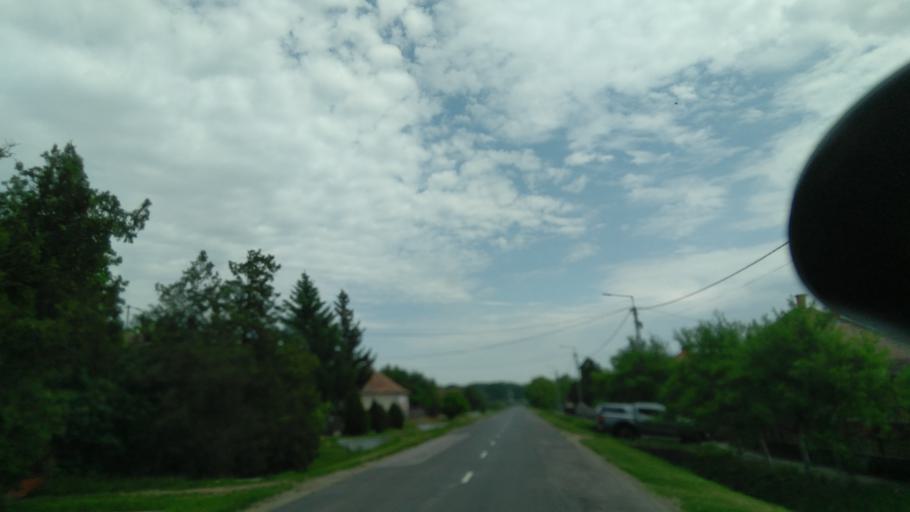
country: HU
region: Hajdu-Bihar
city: Komadi
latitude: 47.0221
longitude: 21.5565
